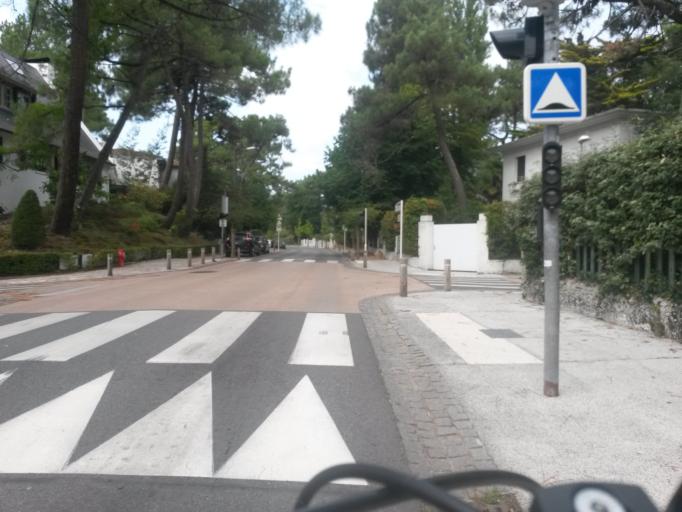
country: FR
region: Pays de la Loire
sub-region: Departement de la Loire-Atlantique
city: La Baule-Escoublac
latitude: 47.2854
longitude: -2.3755
